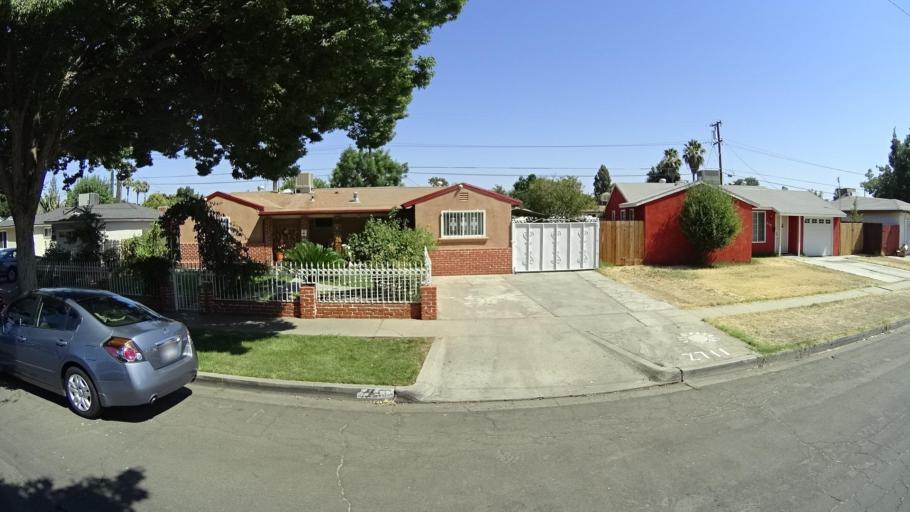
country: US
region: California
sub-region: Fresno County
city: Fresno
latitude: 36.7990
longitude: -119.7787
